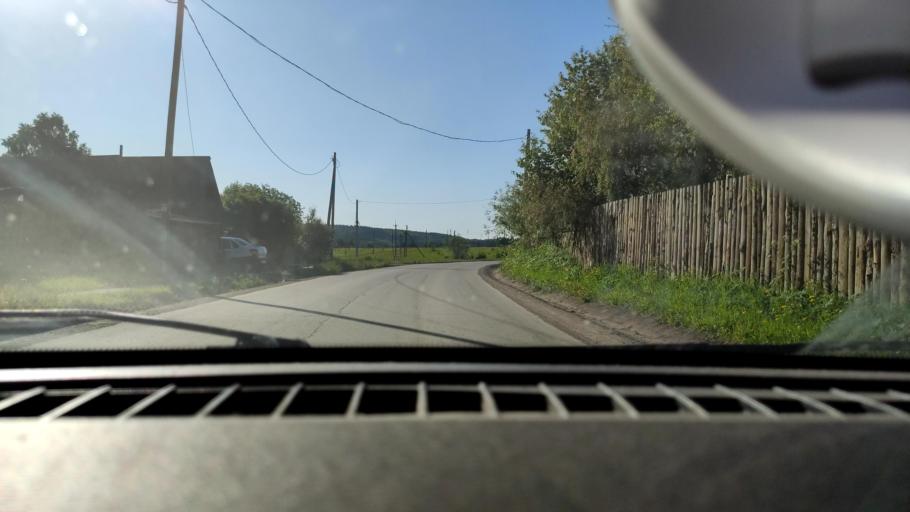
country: RU
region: Perm
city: Novyye Lyady
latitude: 58.1841
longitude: 56.5469
